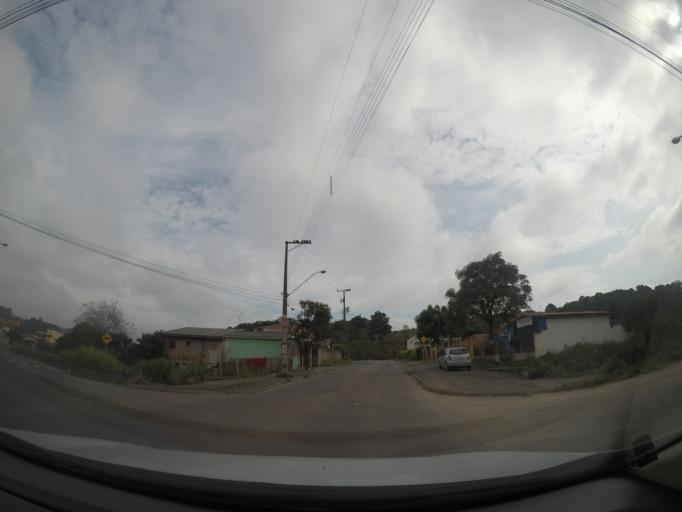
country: BR
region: Parana
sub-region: Colombo
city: Colombo
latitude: -25.3449
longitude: -49.2285
